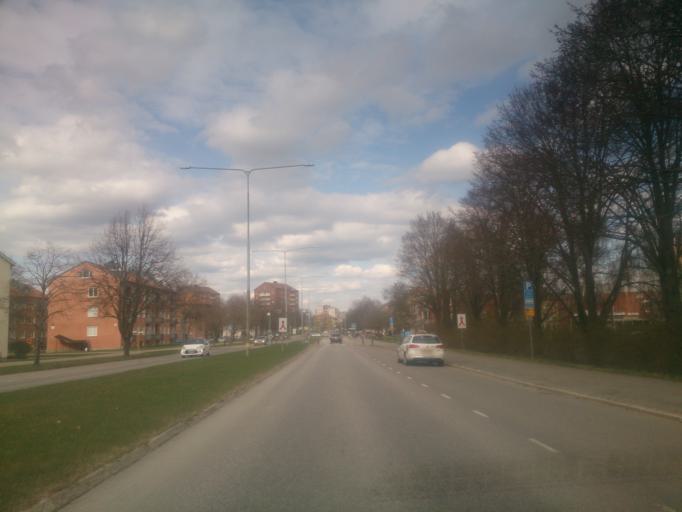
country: SE
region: OEstergoetland
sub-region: Norrkopings Kommun
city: Norrkoping
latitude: 58.5777
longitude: 16.1812
